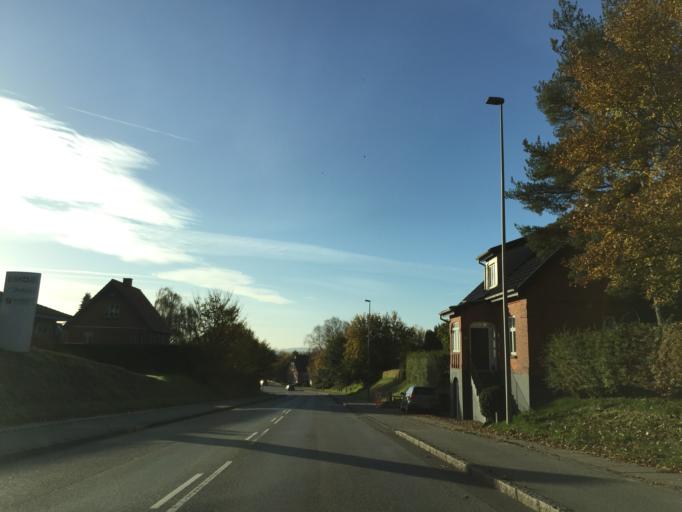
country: DK
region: Central Jutland
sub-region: Skanderborg Kommune
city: Skanderborg
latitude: 56.0453
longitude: 9.9200
